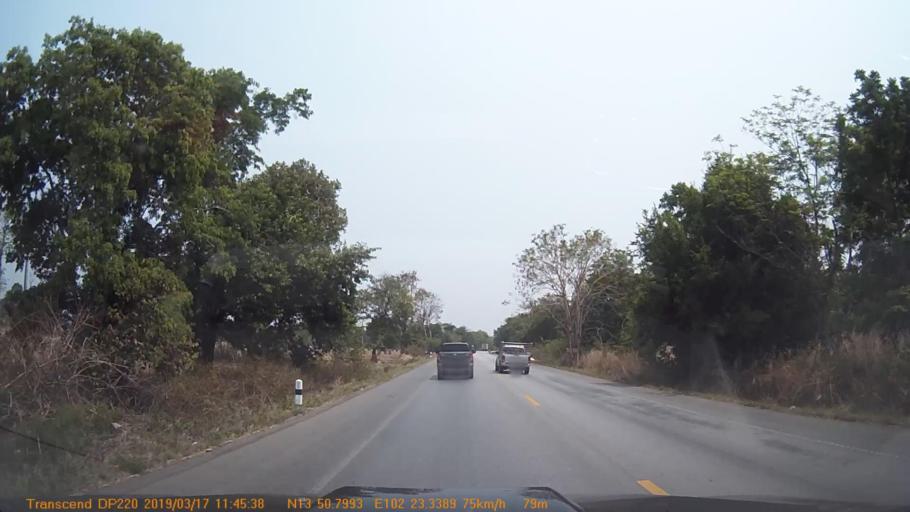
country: TH
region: Sa Kaeo
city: Watthana Nakhon
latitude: 13.8468
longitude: 102.3892
